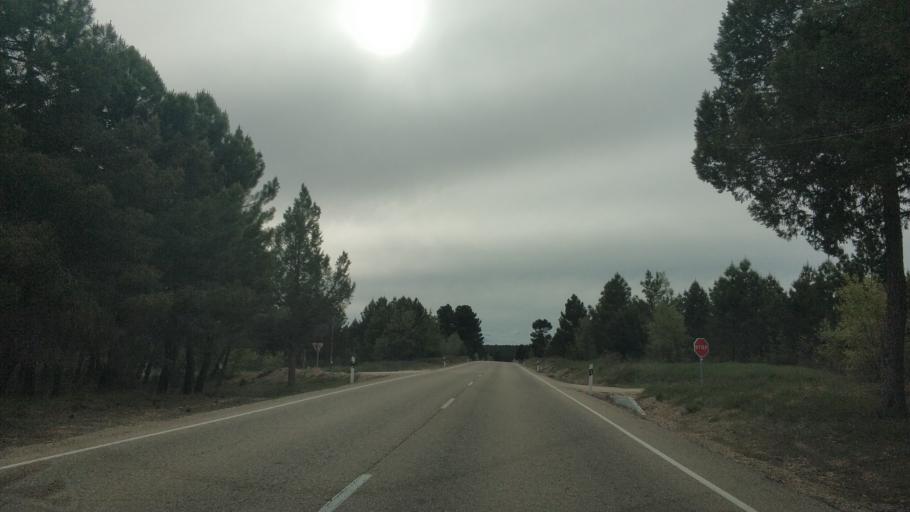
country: ES
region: Castille and Leon
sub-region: Provincia de Soria
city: Bayubas de Abajo
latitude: 41.5095
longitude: -2.9150
